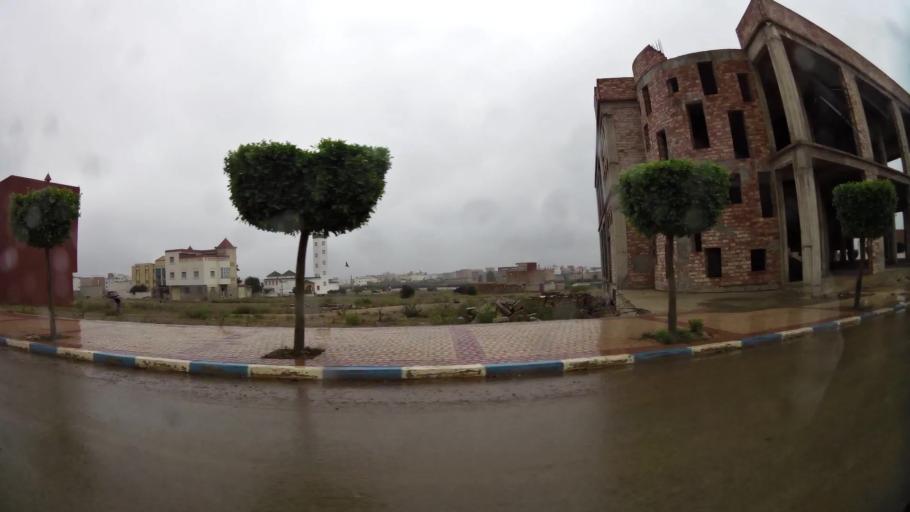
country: MA
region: Taza-Al Hoceima-Taounate
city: Imzourene
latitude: 35.1356
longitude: -3.8492
